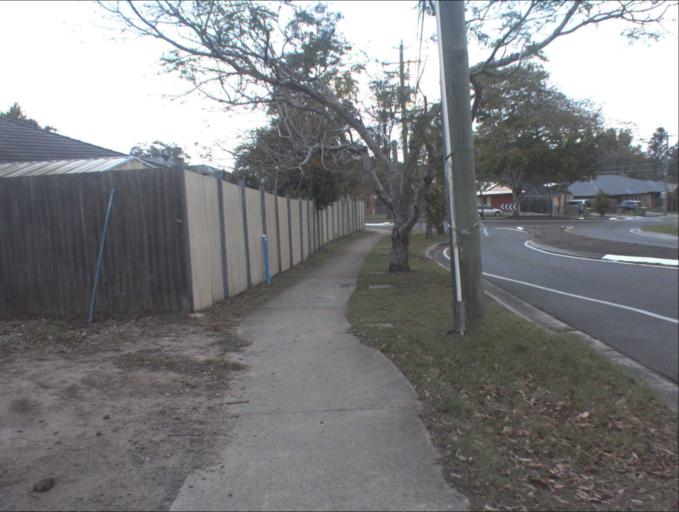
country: AU
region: Queensland
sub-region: Logan
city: Waterford West
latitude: -27.6823
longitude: 153.1331
